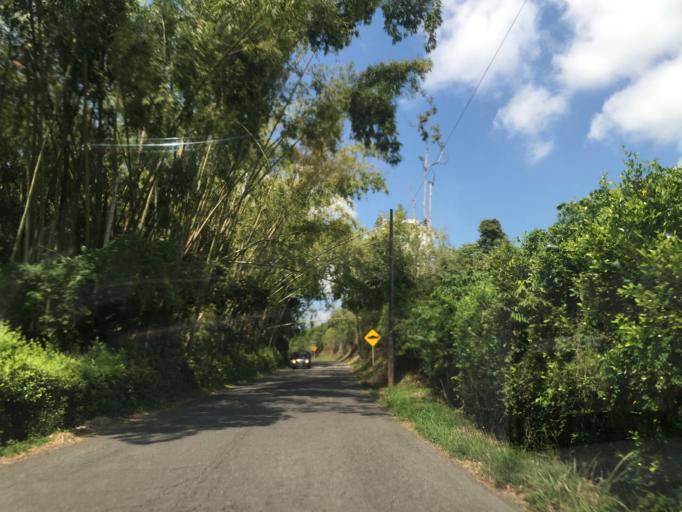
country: CO
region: Valle del Cauca
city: Ulloa
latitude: 4.7399
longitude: -75.7813
